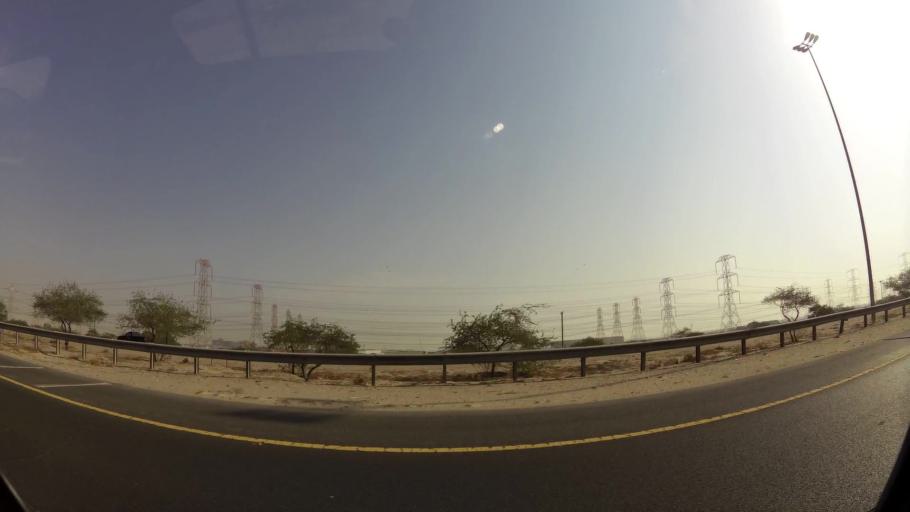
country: KW
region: Al Ahmadi
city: Al Ahmadi
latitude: 28.9699
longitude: 48.1142
